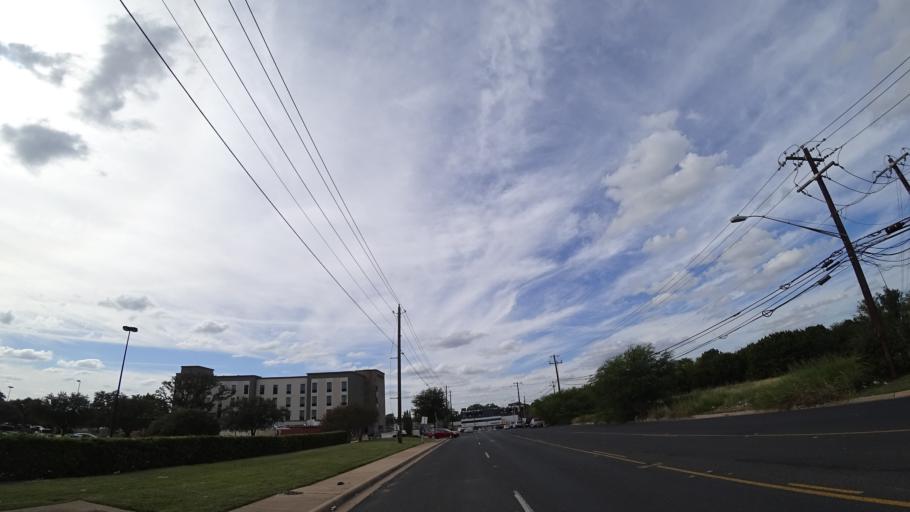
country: US
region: Texas
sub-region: Travis County
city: Austin
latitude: 30.2047
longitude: -97.7567
